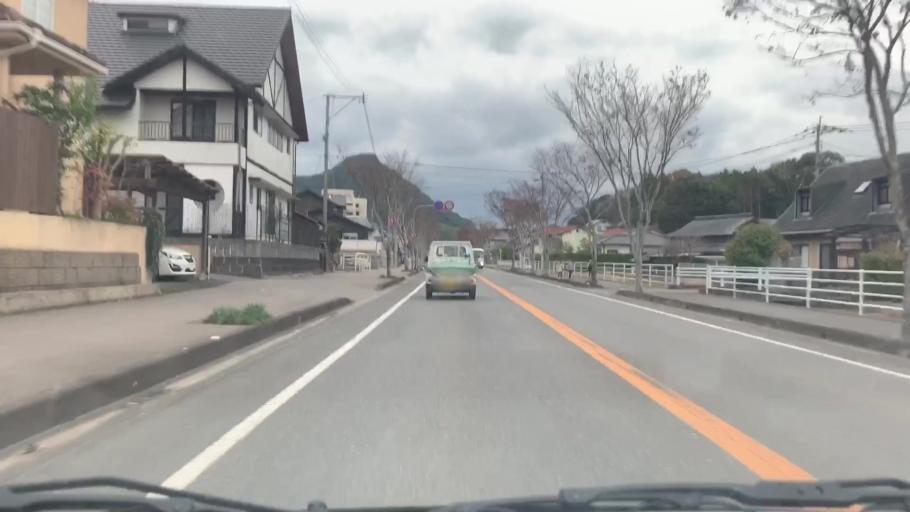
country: JP
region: Saga Prefecture
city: Takeocho-takeo
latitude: 33.1870
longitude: 130.0314
